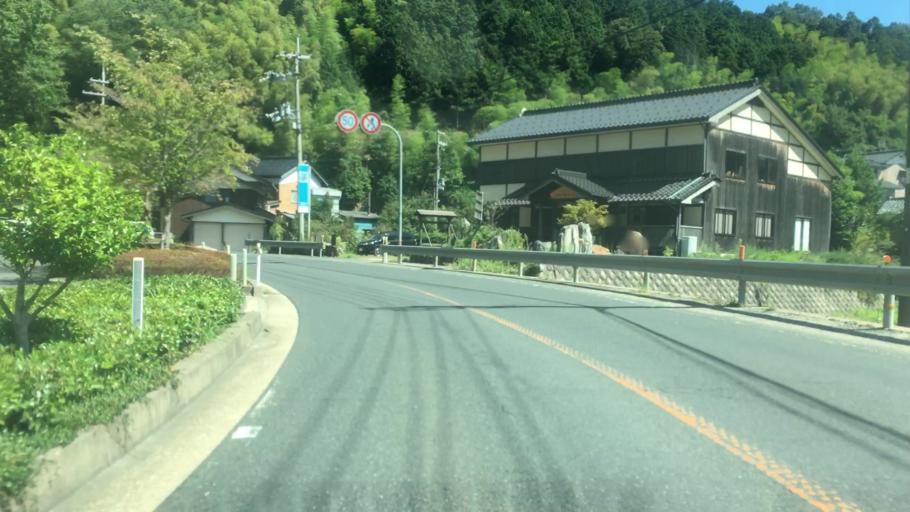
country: JP
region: Hyogo
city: Toyooka
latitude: 35.5941
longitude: 134.9062
